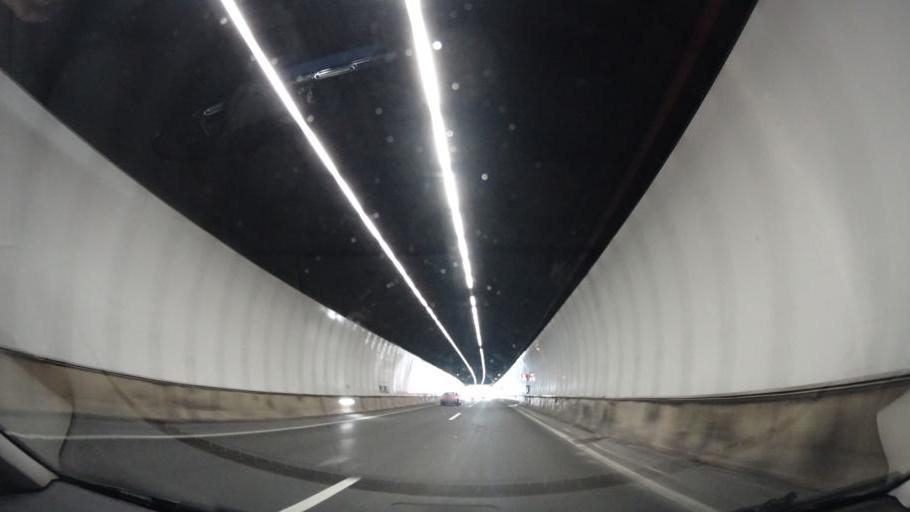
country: ES
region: Basque Country
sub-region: Bizkaia
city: Basauri
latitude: 43.2334
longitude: -2.9050
